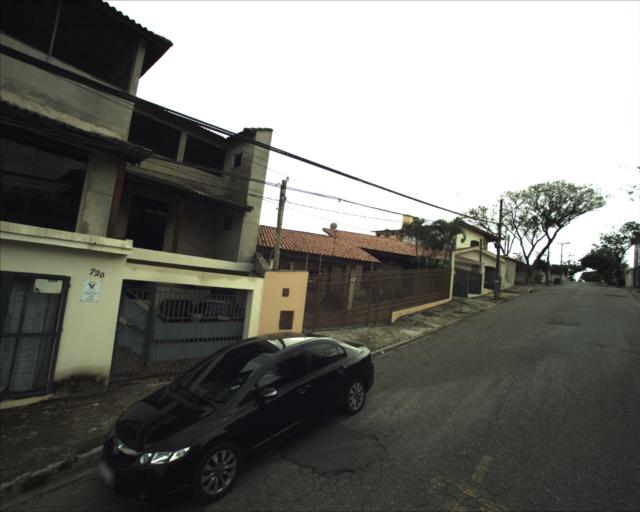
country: BR
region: Sao Paulo
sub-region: Sorocaba
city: Sorocaba
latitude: -23.5083
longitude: -47.4949
